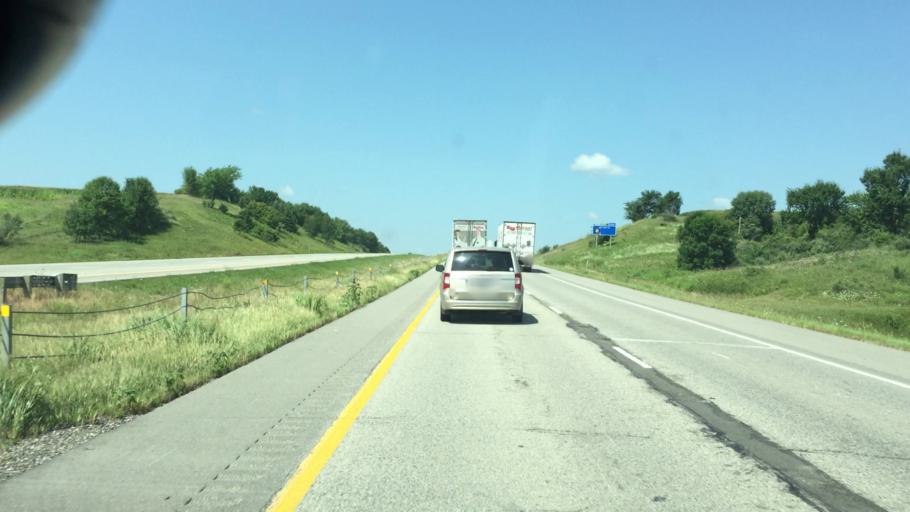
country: US
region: Iowa
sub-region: Poweshiek County
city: Grinnell
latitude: 41.6952
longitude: -92.8450
